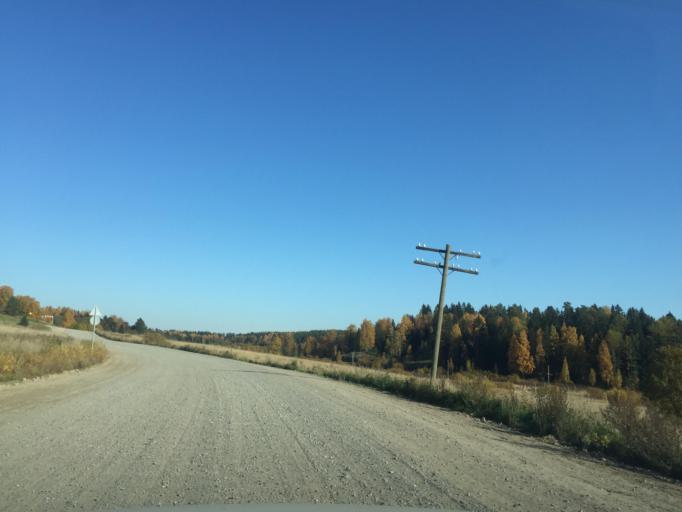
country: RU
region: Leningrad
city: Kuznechnoye
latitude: 61.3062
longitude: 29.9282
